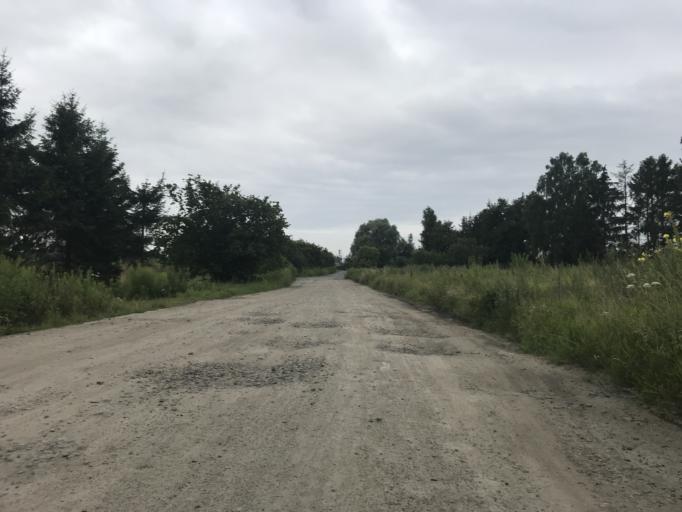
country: PL
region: Pomeranian Voivodeship
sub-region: Gdansk
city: Gdansk
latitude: 54.3397
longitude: 18.6833
